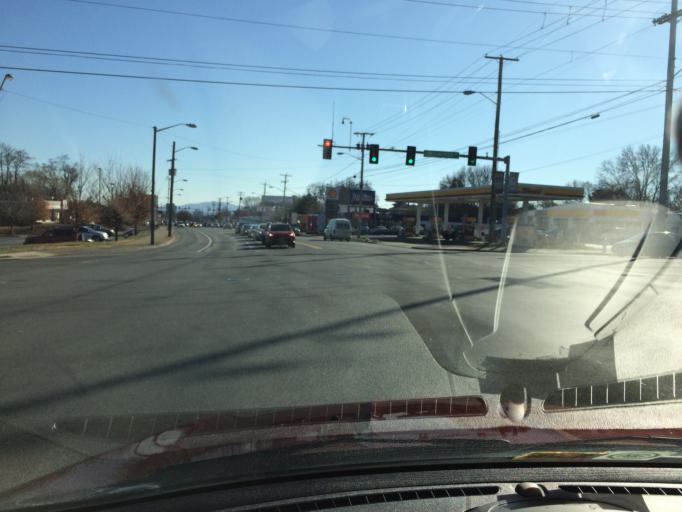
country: US
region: Virginia
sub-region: Roanoke County
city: Hollins
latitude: 37.3167
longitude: -79.9552
